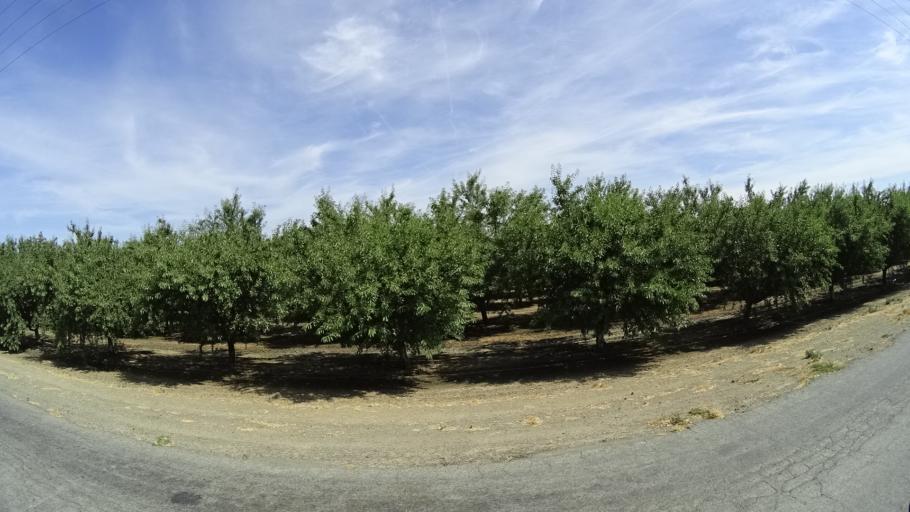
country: US
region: California
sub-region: Kings County
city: Hanford
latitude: 36.3572
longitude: -119.5856
